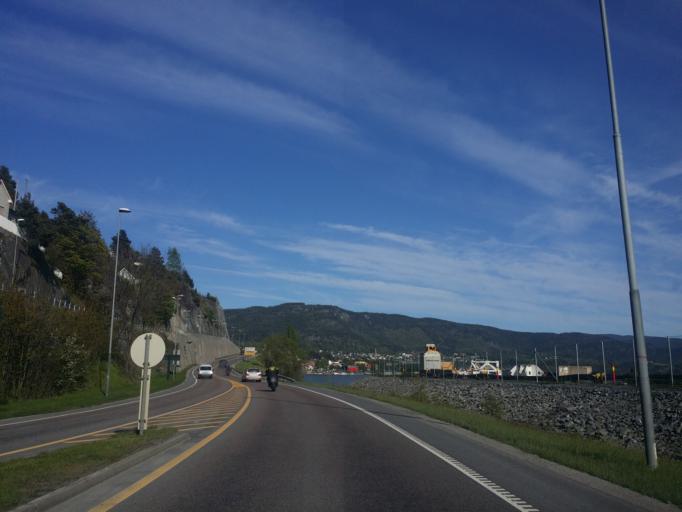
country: NO
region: Telemark
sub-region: Notodden
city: Notodden
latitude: 59.5612
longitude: 9.2336
